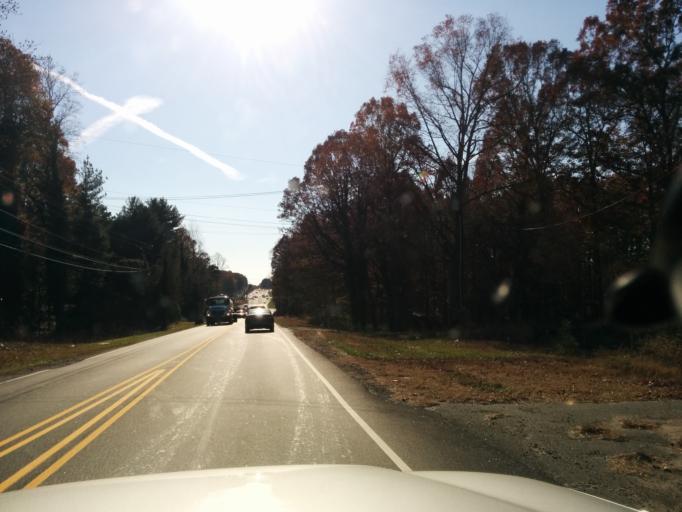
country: US
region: North Carolina
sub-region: Iredell County
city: Mooresville
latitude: 35.5598
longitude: -80.8511
